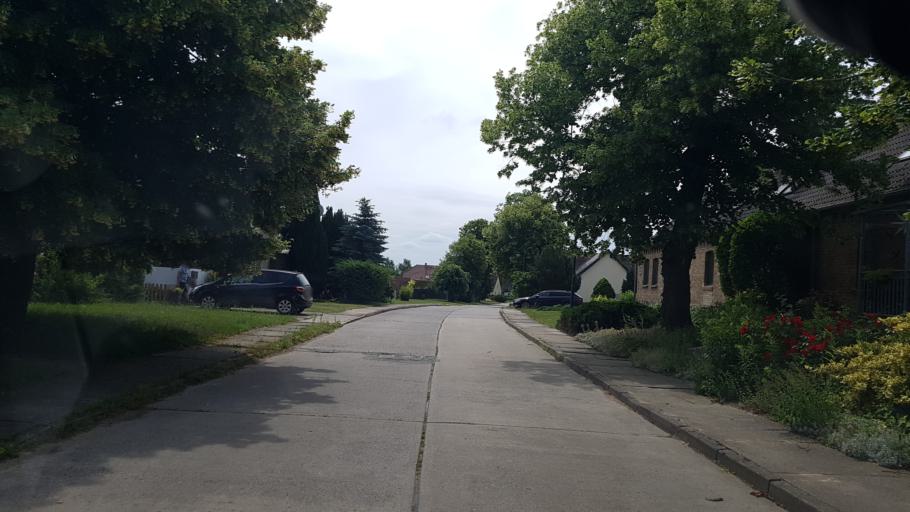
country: DE
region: Mecklenburg-Vorpommern
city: Strasburg
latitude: 53.4489
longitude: 13.8068
